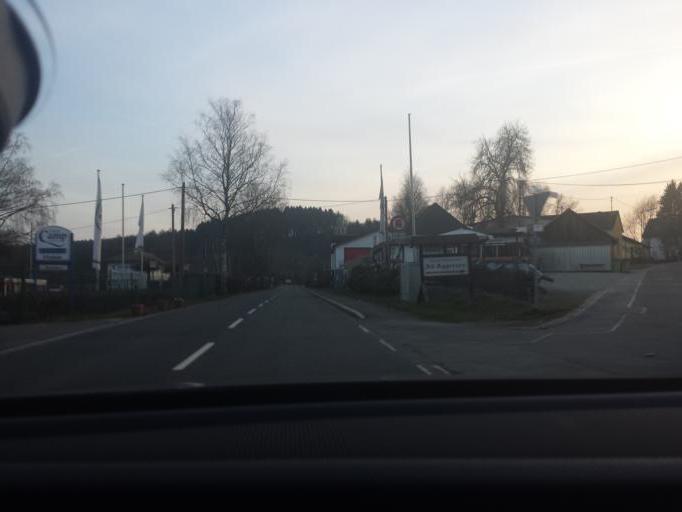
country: DE
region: North Rhine-Westphalia
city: Bergneustadt
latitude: 51.0532
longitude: 7.6273
